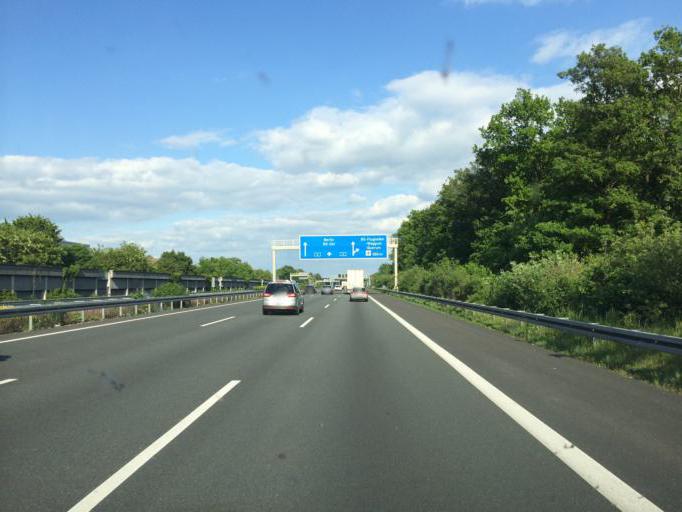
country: DE
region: Lower Saxony
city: Braunschweig
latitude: 52.3131
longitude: 10.5454
